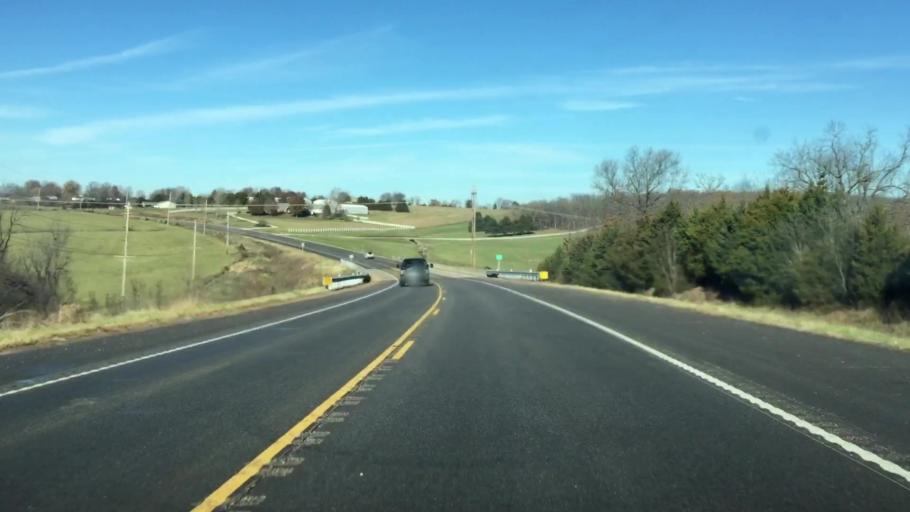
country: US
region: Missouri
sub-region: Miller County
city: Eldon
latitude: 38.3699
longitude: -92.6167
